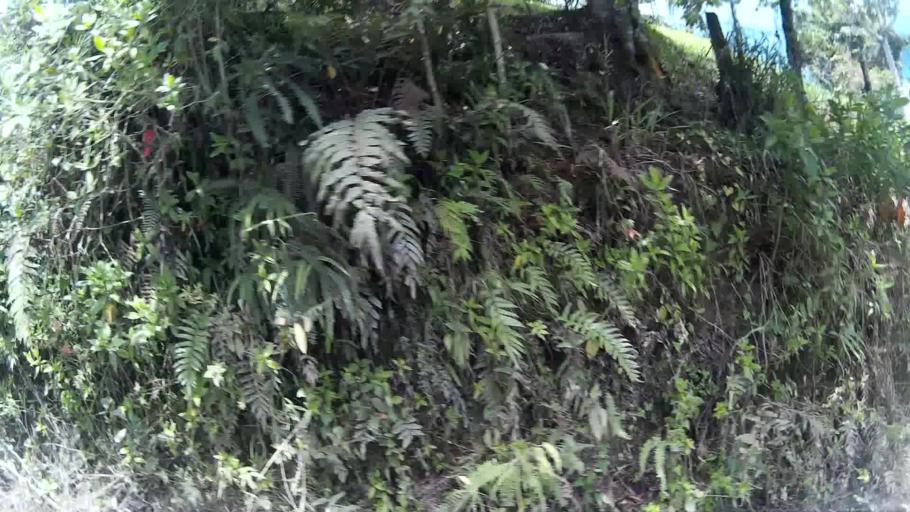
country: CO
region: Quindio
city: Filandia
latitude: 4.7130
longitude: -75.6603
